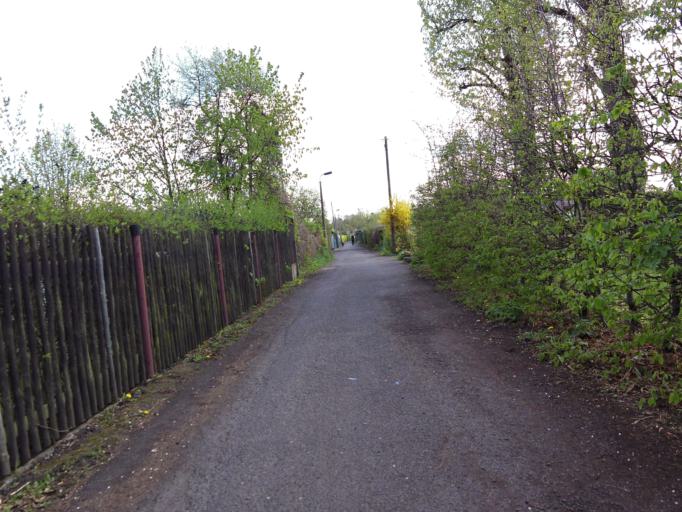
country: DE
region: Saxony
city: Leipzig
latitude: 51.3401
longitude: 12.4225
